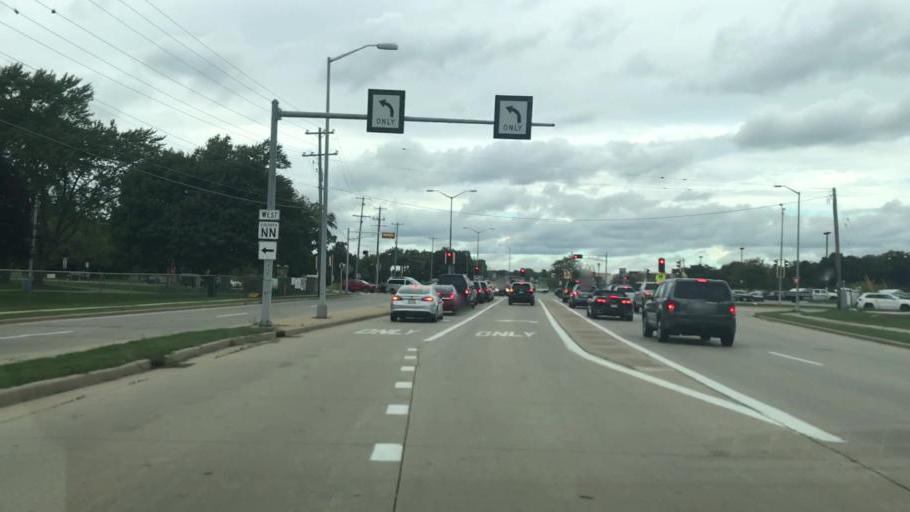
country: US
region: Wisconsin
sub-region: Waukesha County
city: Mukwonago
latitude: 42.8733
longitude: -88.3374
